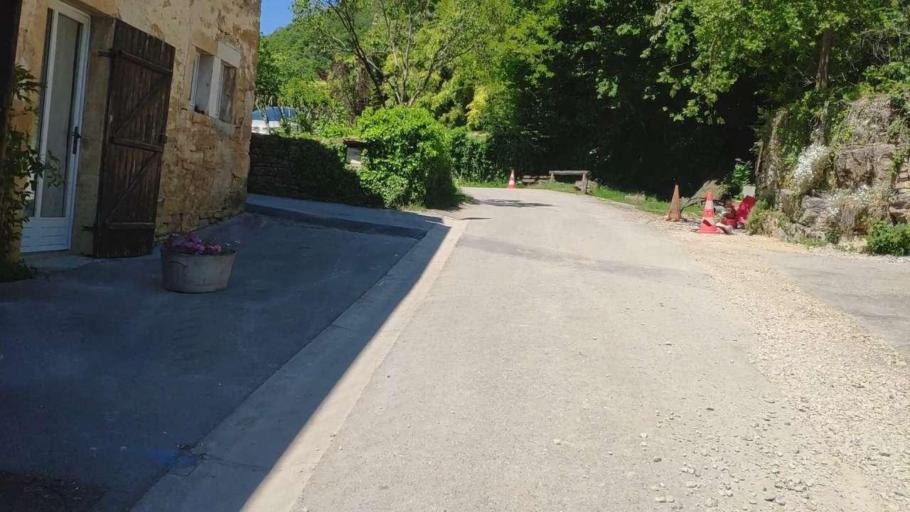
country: FR
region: Franche-Comte
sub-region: Departement du Jura
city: Perrigny
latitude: 46.7422
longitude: 5.6320
